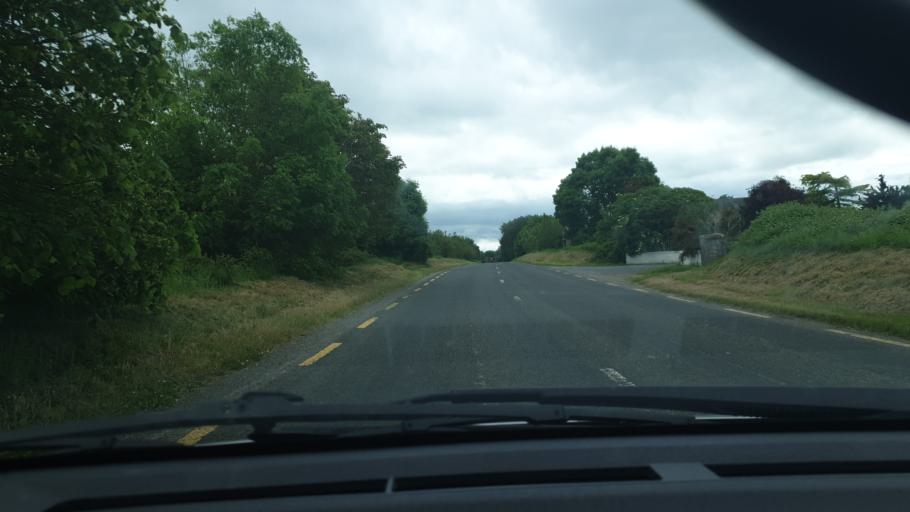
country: IE
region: Munster
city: Cahir
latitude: 52.3939
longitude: -7.9109
